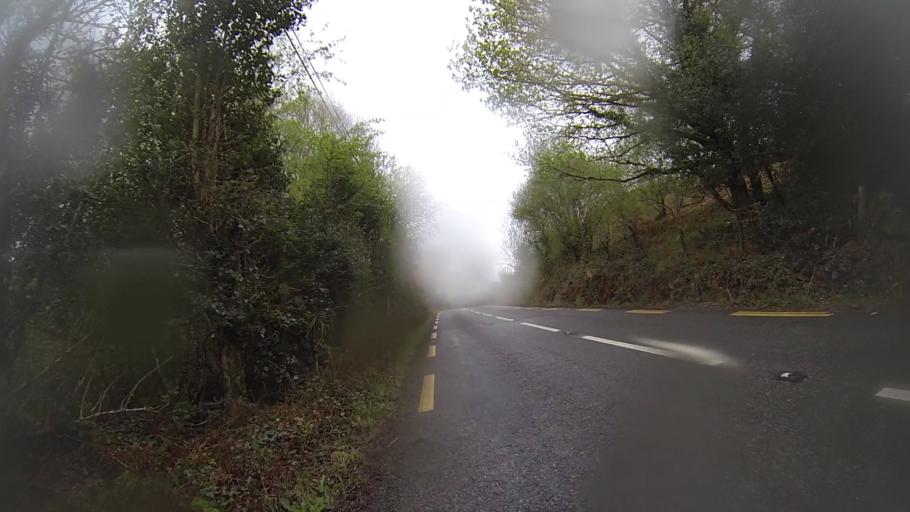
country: IE
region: Munster
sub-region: Ciarrai
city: Kenmare
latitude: 51.8183
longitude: -9.5319
